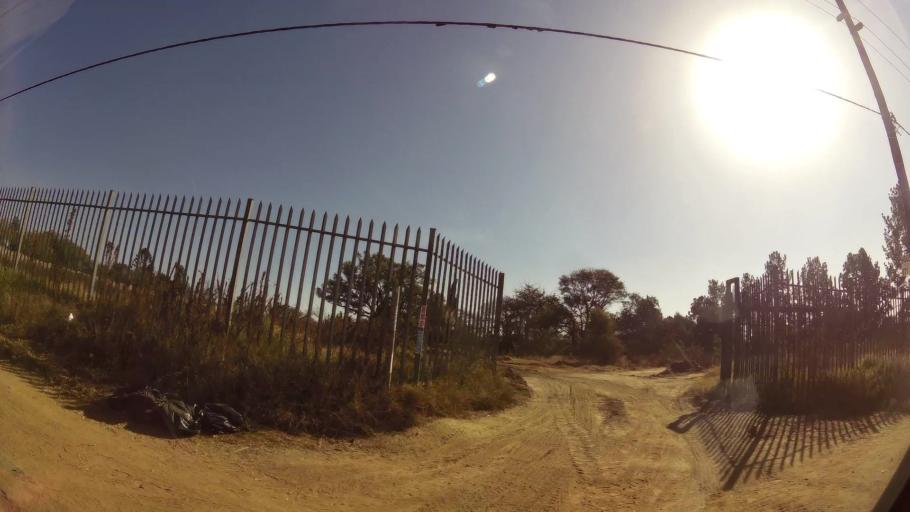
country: ZA
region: Gauteng
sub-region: City of Johannesburg Metropolitan Municipality
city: Diepsloot
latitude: -26.0143
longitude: 27.9432
